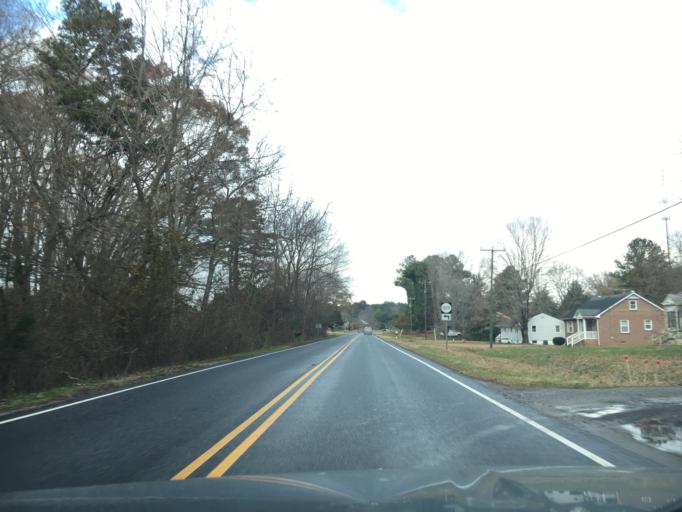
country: US
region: Virginia
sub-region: Prince Edward County
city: Farmville
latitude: 37.3232
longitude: -78.3865
